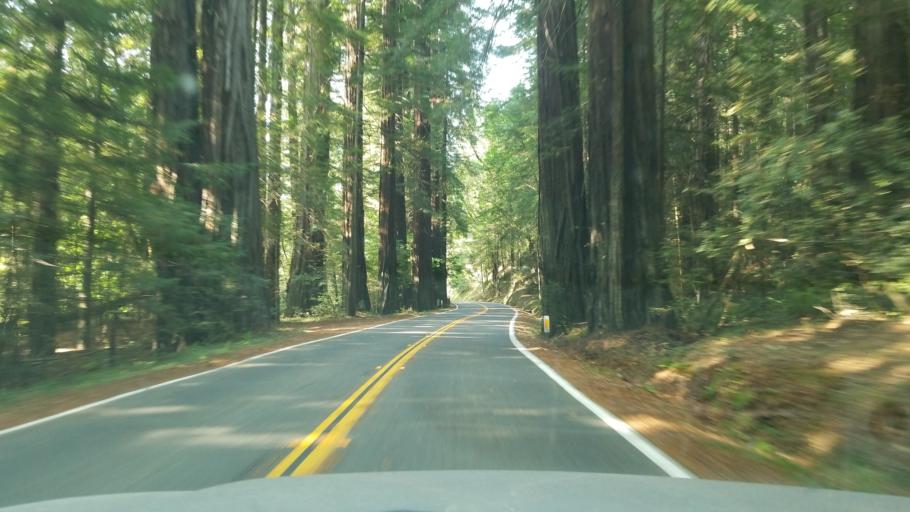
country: US
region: California
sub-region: Humboldt County
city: Redway
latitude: 40.2709
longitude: -123.8501
